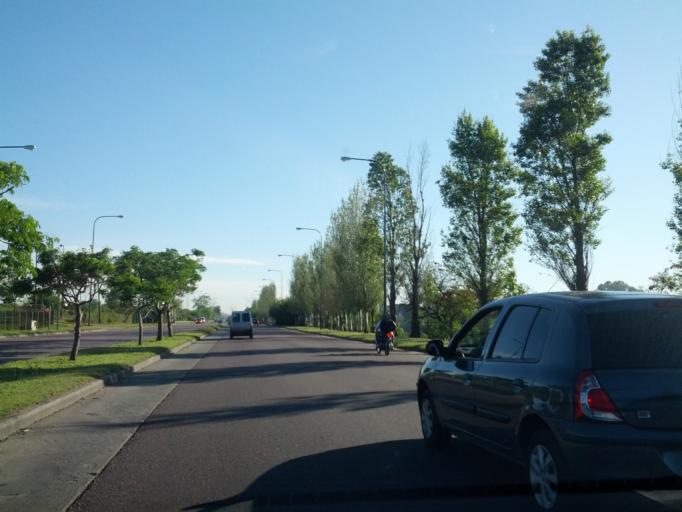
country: AR
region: Buenos Aires F.D.
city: Villa Lugano
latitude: -34.6831
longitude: -58.4430
